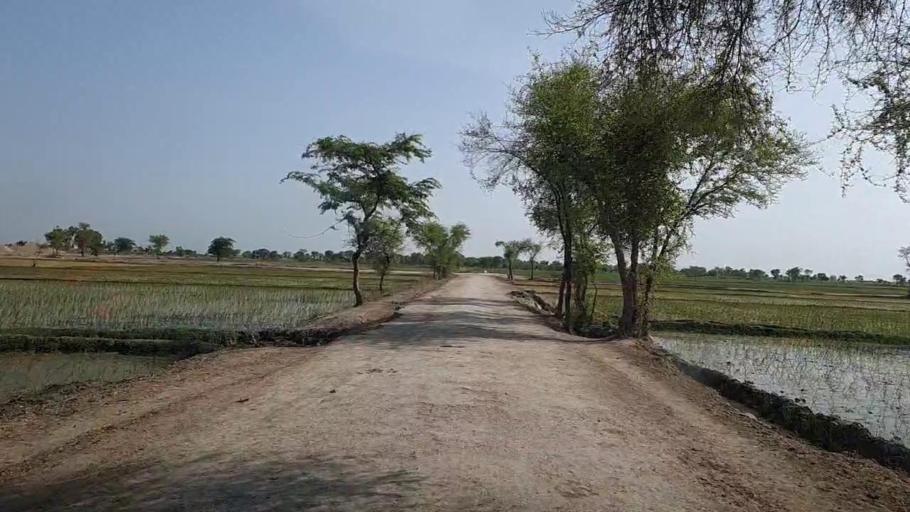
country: PK
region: Sindh
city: Sita Road
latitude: 27.0926
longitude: 67.8482
